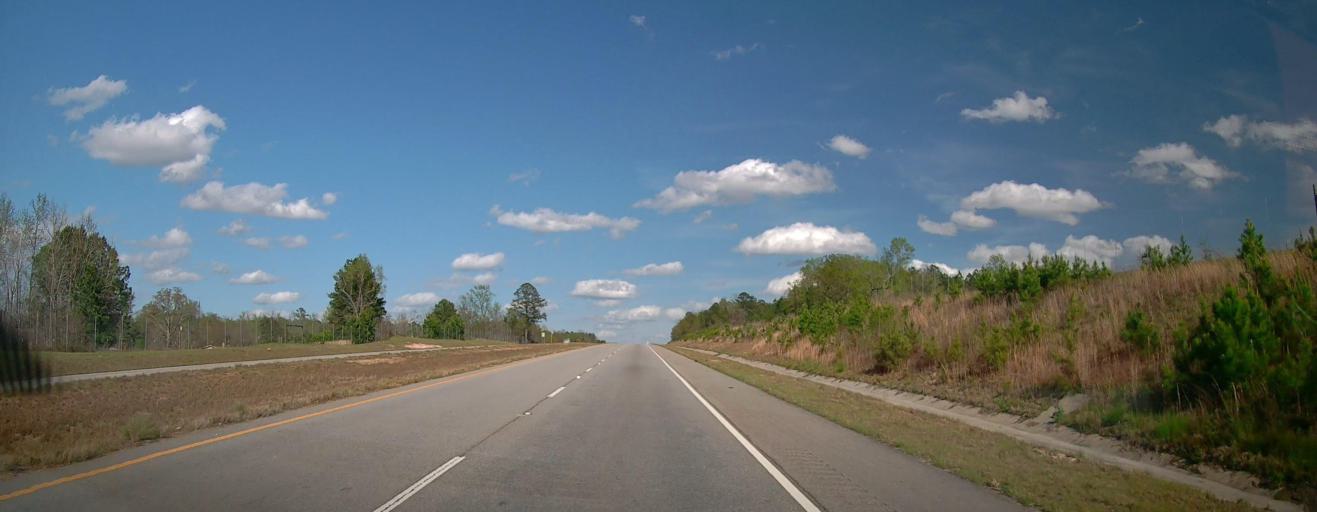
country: US
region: Georgia
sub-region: Baldwin County
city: Hardwick
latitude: 33.0368
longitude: -83.1507
